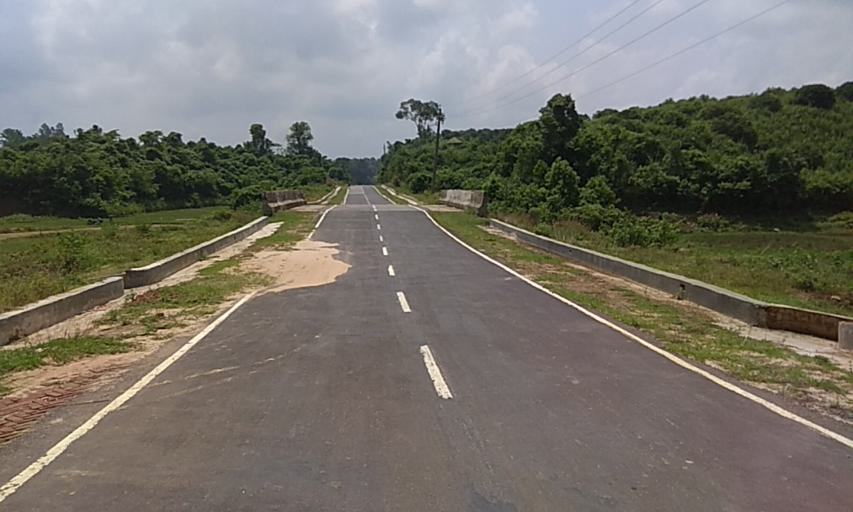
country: BD
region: Chittagong
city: Manikchari
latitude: 22.9377
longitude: 91.9049
